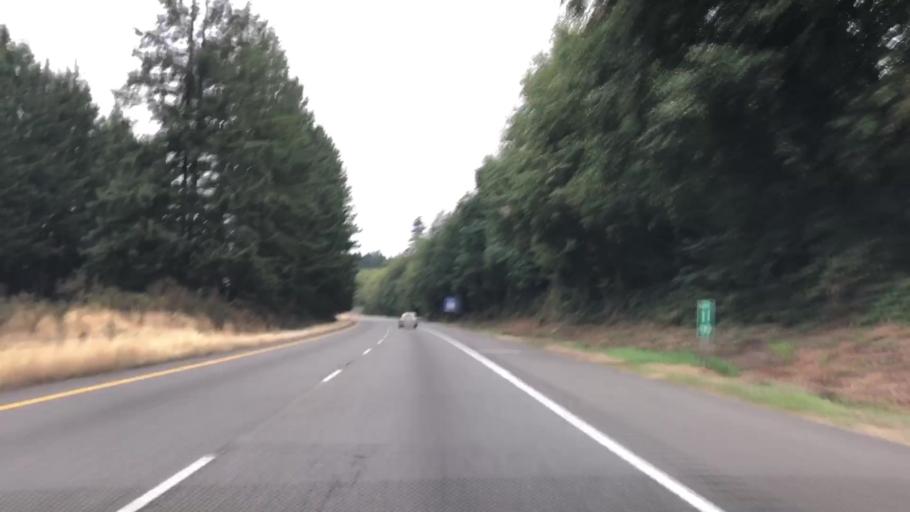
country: US
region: Washington
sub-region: Kitsap County
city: Burley
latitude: 47.4162
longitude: -122.6230
